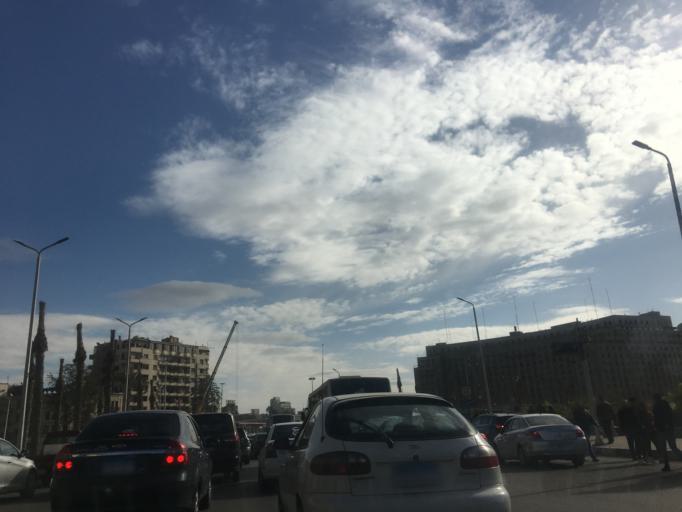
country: EG
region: Muhafazat al Qahirah
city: Cairo
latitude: 30.0458
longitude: 31.2349
